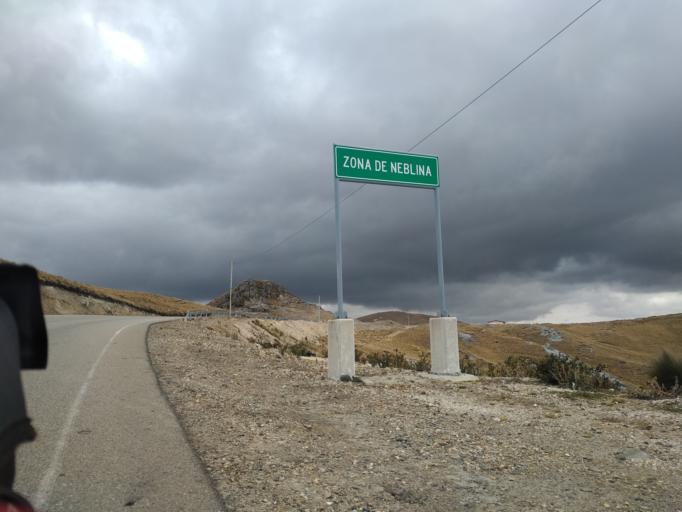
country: PE
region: La Libertad
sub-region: Provincia de Santiago de Chuco
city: Quiruvilca
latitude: -7.9894
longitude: -78.2845
